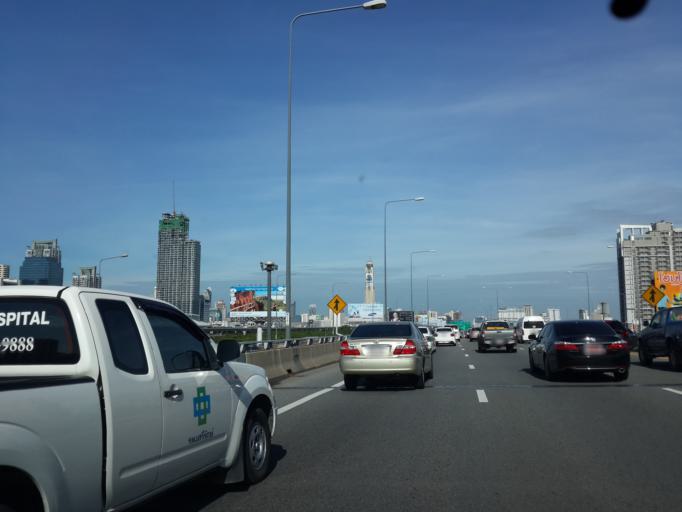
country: TH
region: Bangkok
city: Din Daeng
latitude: 13.7529
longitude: 100.5650
